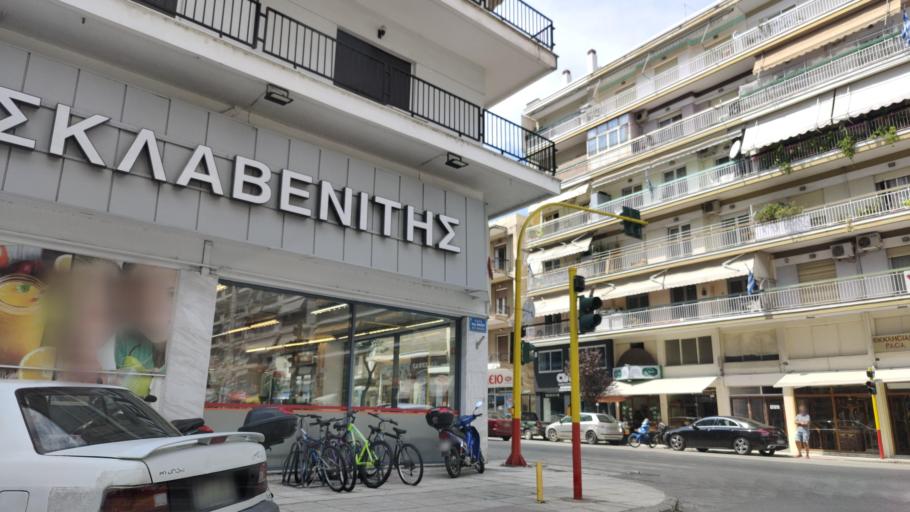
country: GR
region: Central Macedonia
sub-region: Nomos Serron
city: Serres
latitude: 41.0875
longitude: 23.5410
